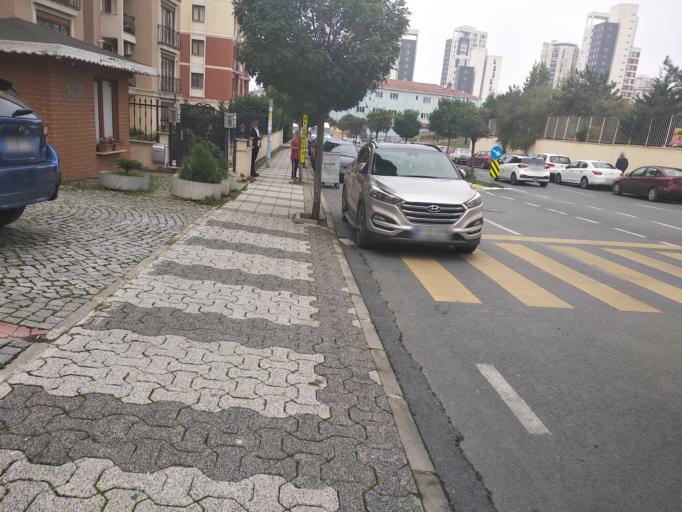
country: TR
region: Istanbul
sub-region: Atasehir
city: Atasehir
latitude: 40.9833
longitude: 29.1240
